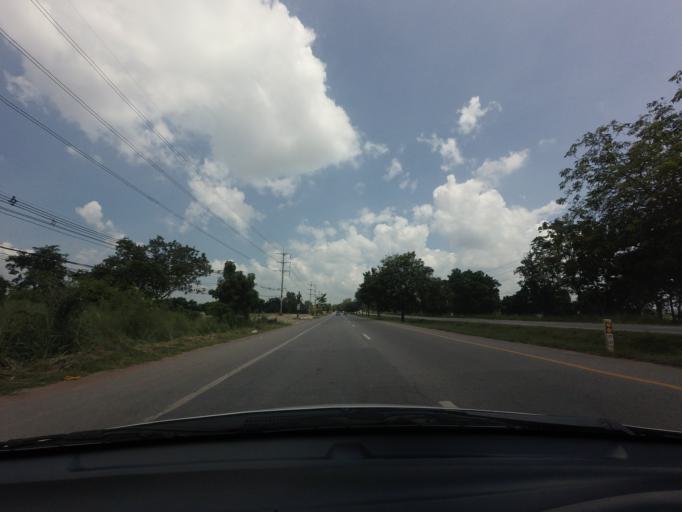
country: TH
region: Chachoengsao
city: Sanam Chai Khet
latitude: 13.7889
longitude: 101.5358
